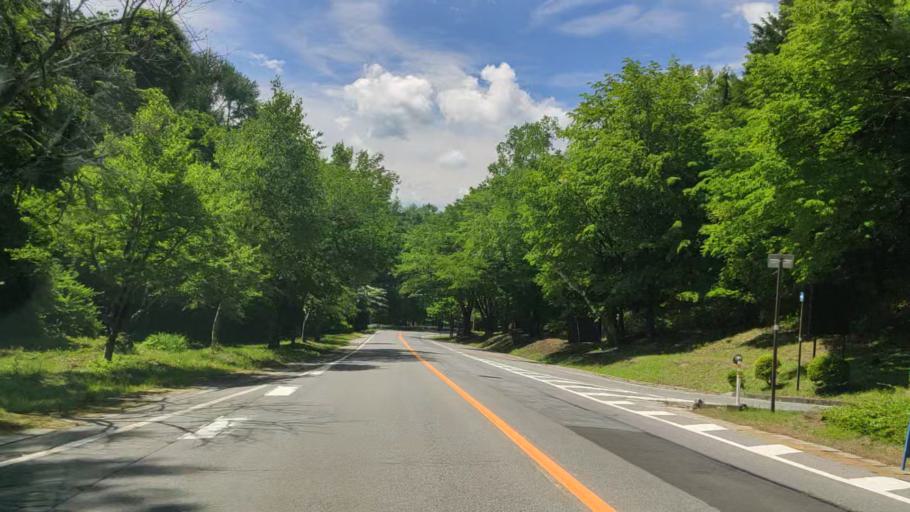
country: JP
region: Nagano
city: Chino
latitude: 36.0423
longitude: 138.2481
